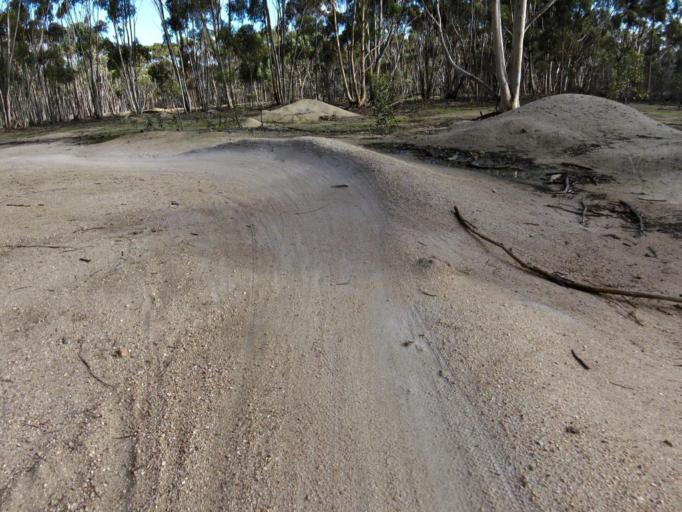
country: AU
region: Victoria
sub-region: Greater Geelong
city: Lara
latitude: -37.9395
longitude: 144.4081
